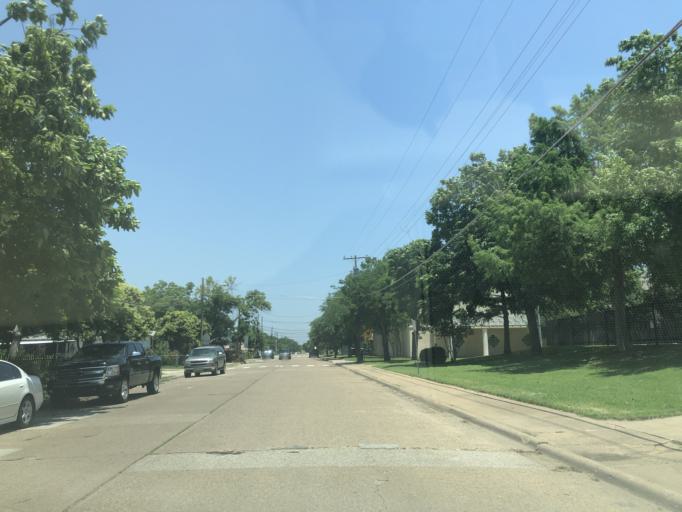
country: US
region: Texas
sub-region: Dallas County
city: Dallas
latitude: 32.7799
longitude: -96.8397
